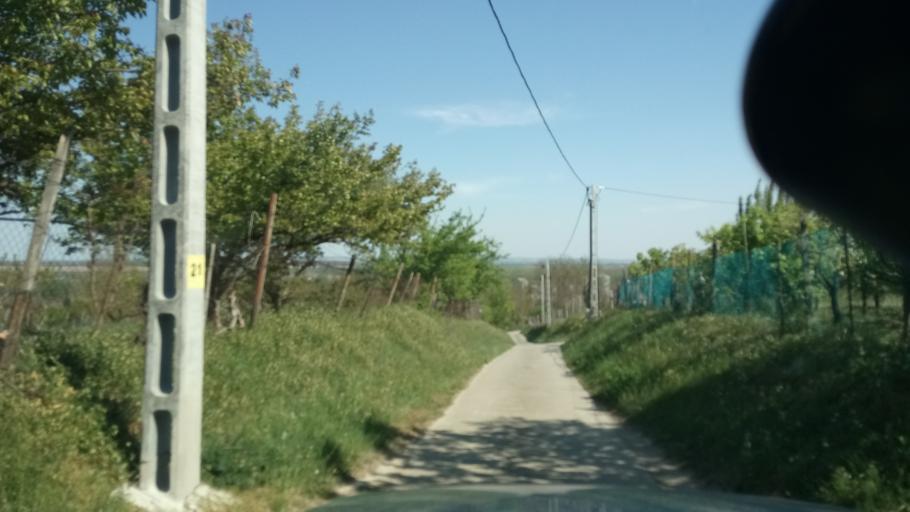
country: HU
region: Zala
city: Sarmellek
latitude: 46.7014
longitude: 17.0992
